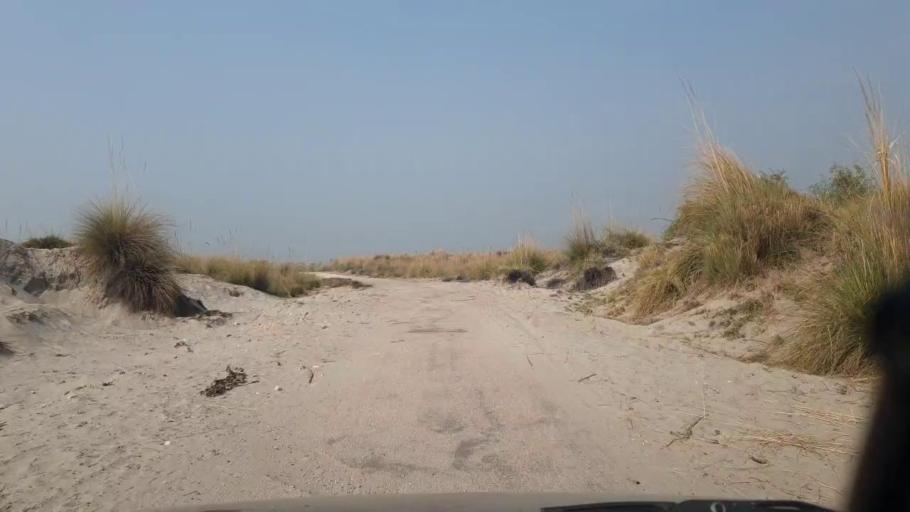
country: PK
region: Sindh
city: Shahdadpur
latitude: 26.0343
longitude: 68.5236
